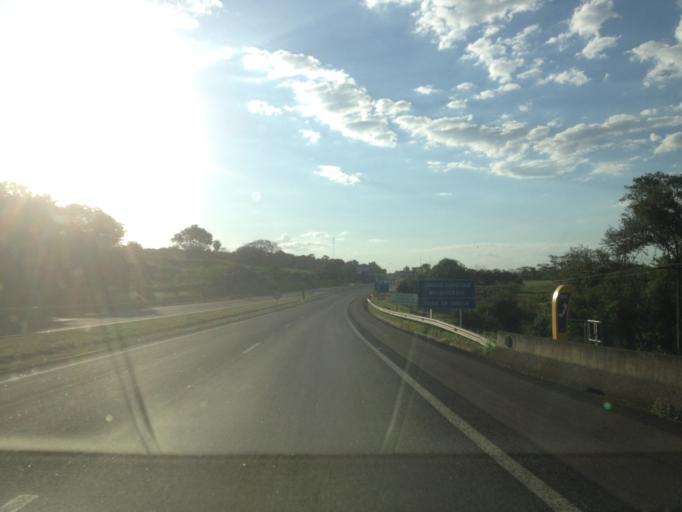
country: BR
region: Sao Paulo
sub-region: Brotas
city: Brotas
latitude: -22.2599
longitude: -48.2400
